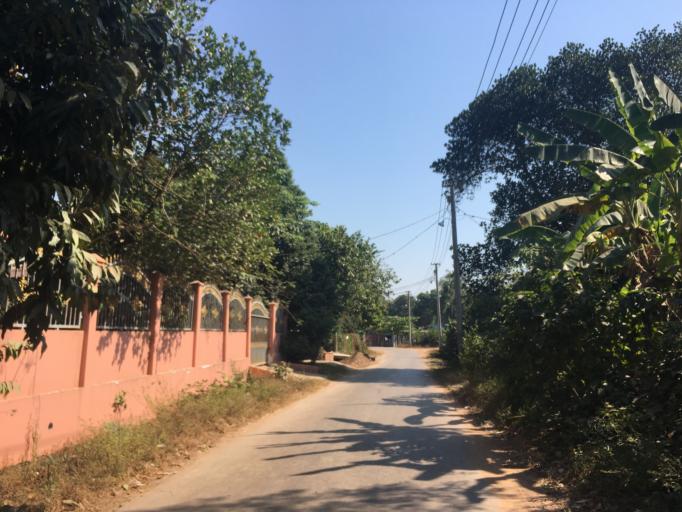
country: MM
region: Mon
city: Mawlamyine
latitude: 16.4316
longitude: 97.7041
